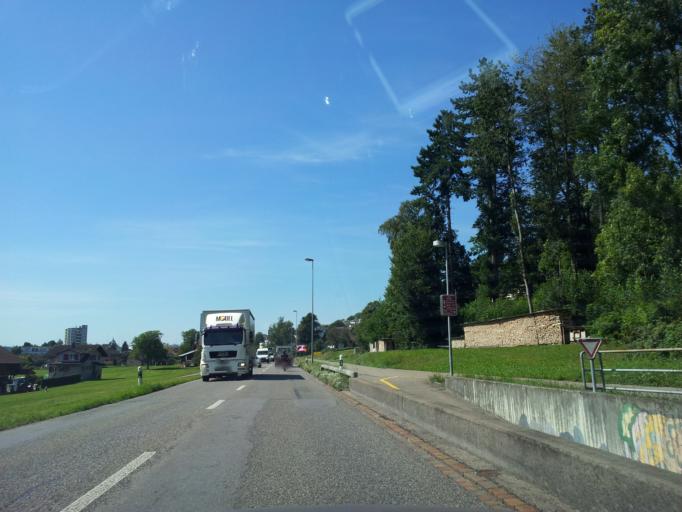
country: CH
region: Saint Gallen
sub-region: Wahlkreis See-Gaster
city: Jona
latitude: 47.2299
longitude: 8.8574
